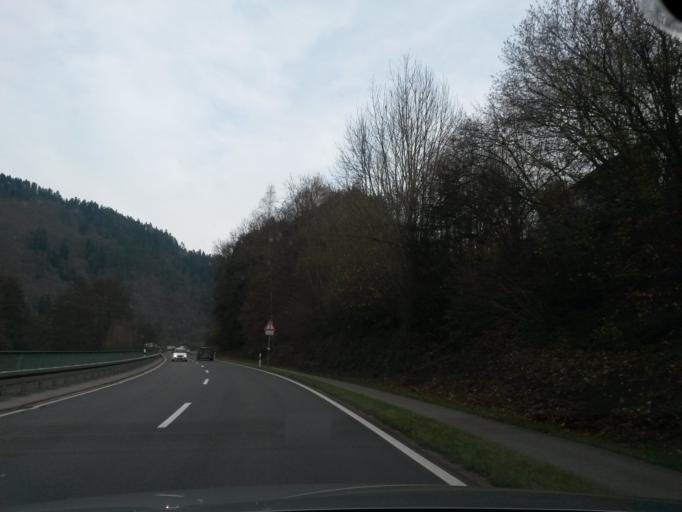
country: DE
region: Baden-Wuerttemberg
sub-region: Freiburg Region
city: Schenkenzell
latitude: 48.2976
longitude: 8.3570
